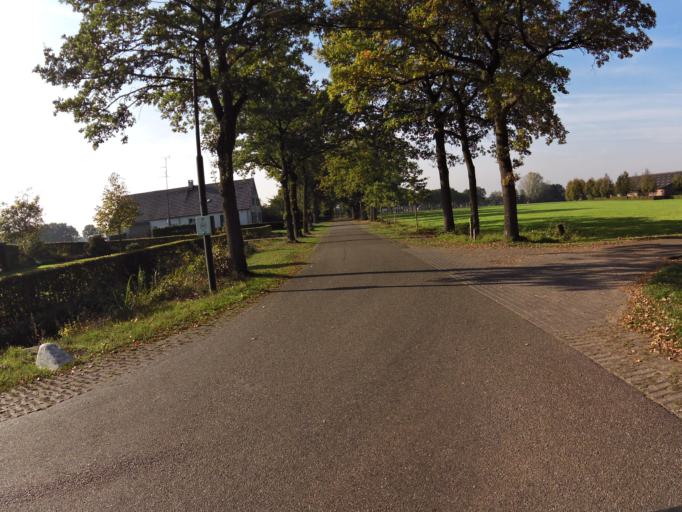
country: NL
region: North Brabant
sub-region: Gemeente Helmond
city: Helmond
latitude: 51.5260
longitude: 5.6927
